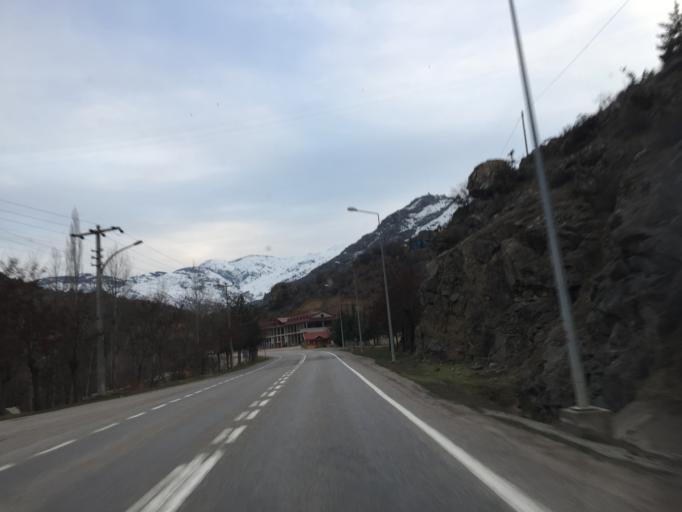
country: TR
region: Gumushane
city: Gumushkhane
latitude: 40.4844
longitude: 39.4626
